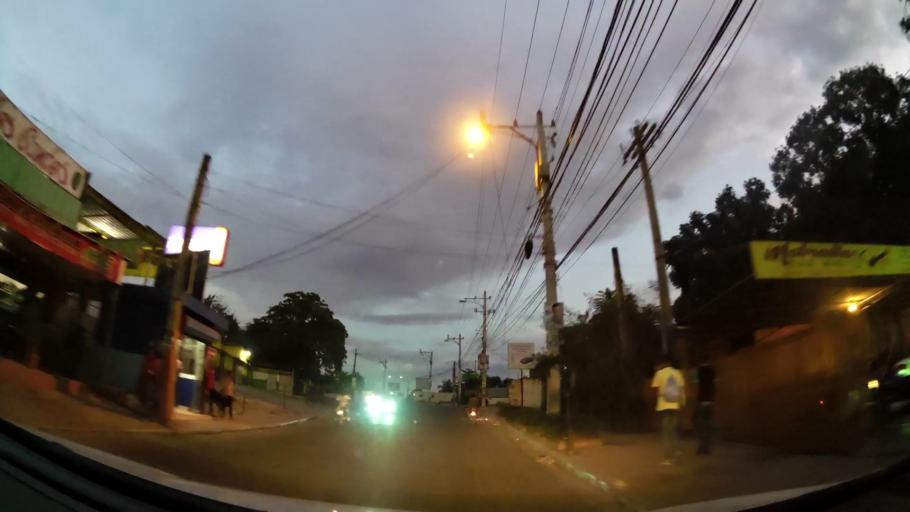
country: DO
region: Santo Domingo
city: Santo Domingo Oeste
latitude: 18.5213
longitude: -70.0169
